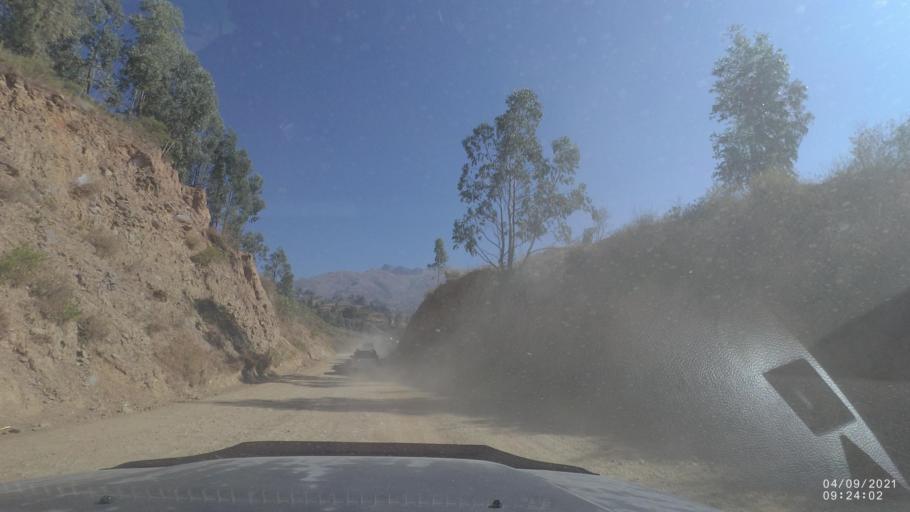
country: BO
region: Cochabamba
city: Sipe Sipe
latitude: -17.3610
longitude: -66.3673
